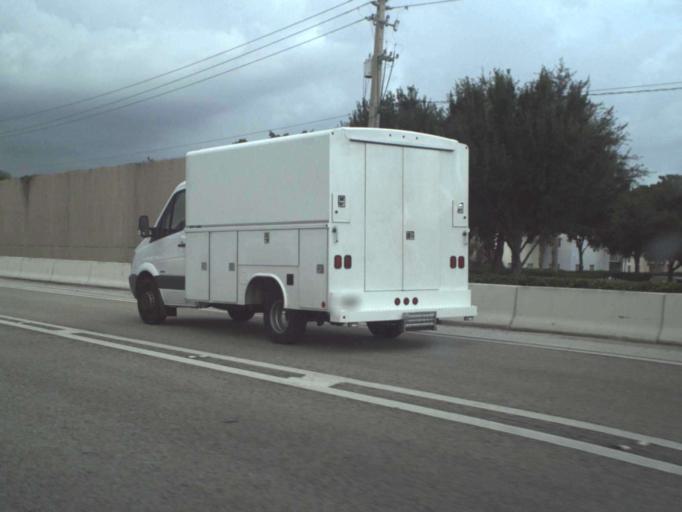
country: US
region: Florida
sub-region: Palm Beach County
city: West Palm Beach
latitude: 26.7094
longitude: -80.0779
